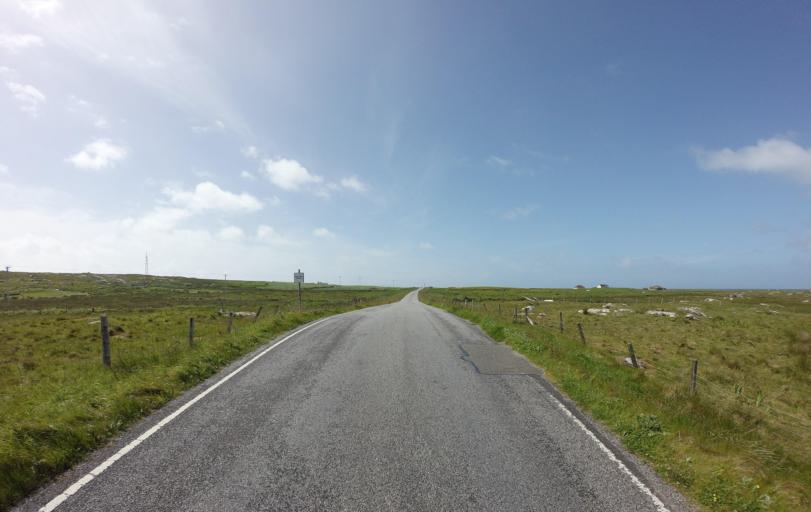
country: GB
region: Scotland
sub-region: Eilean Siar
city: Isle of South Uist
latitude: 57.1131
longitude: -7.3676
